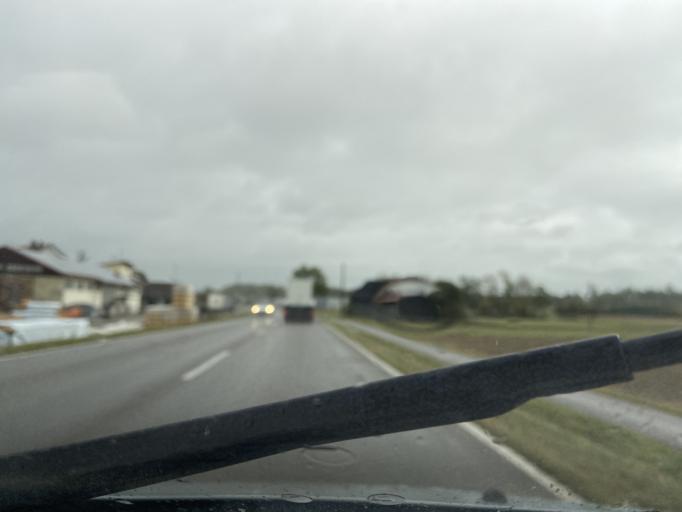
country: DE
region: Baden-Wuerttemberg
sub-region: Tuebingen Region
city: Ennetach
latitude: 48.0398
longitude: 9.3109
